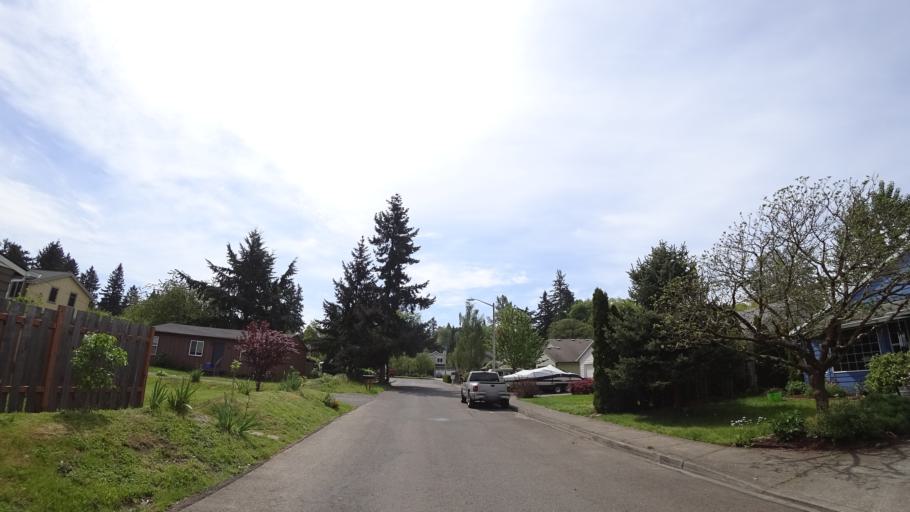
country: US
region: Oregon
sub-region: Clackamas County
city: Milwaukie
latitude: 45.4535
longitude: -122.6058
